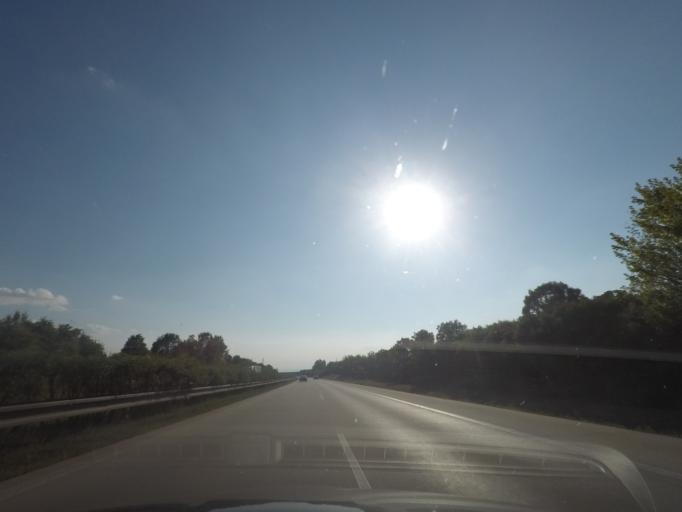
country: CZ
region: Olomoucky
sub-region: Okres Olomouc
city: Velka Bystrice
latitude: 49.5743
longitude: 17.3563
